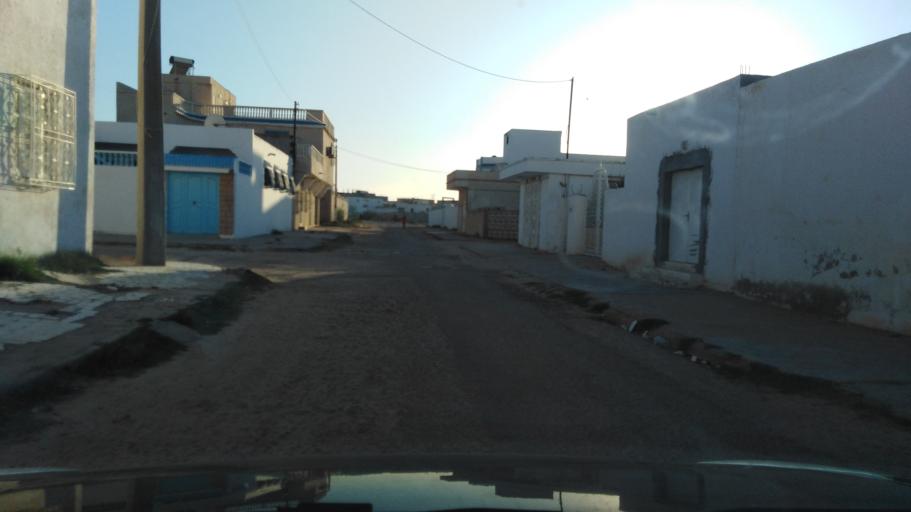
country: TN
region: Qabis
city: Gabes
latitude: 33.9552
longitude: 10.0127
